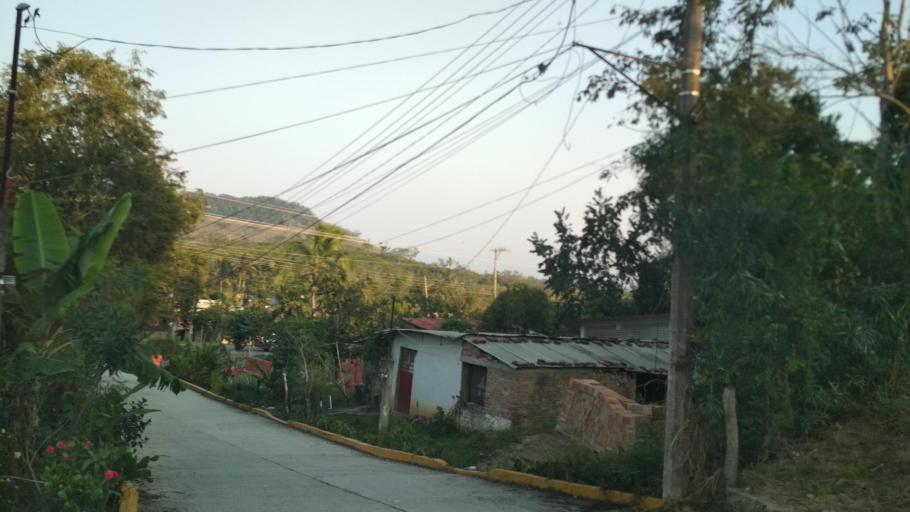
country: MM
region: Shan
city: Taunggyi
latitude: 20.4092
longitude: 97.3378
